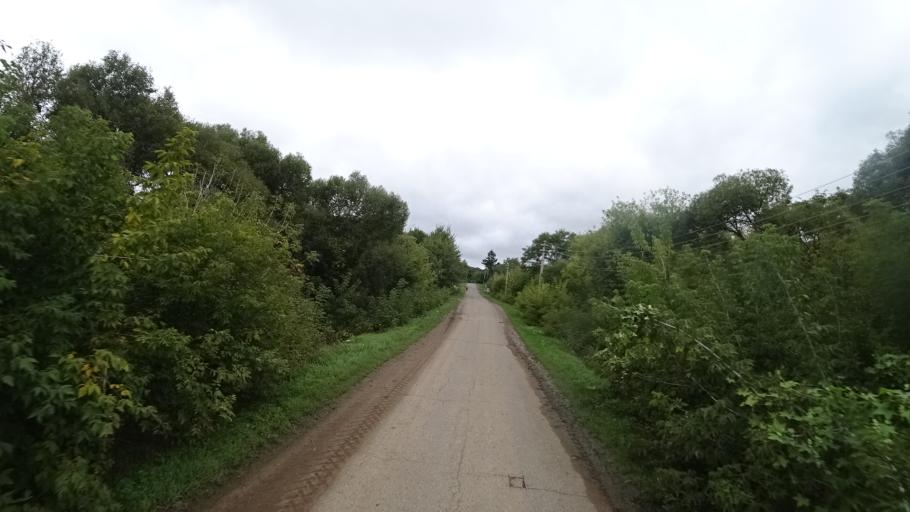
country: RU
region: Primorskiy
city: Chernigovka
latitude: 44.4555
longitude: 132.5890
